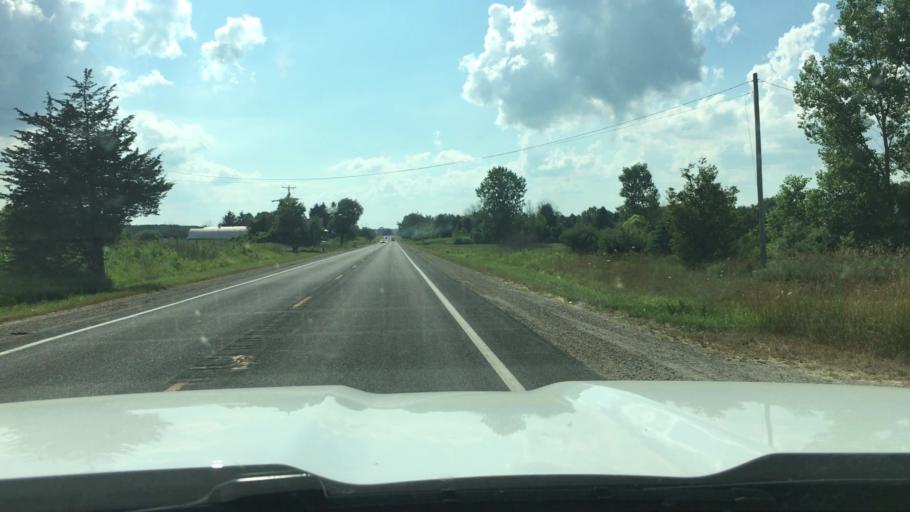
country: US
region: Michigan
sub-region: Montcalm County
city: Stanton
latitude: 43.1776
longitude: -85.0374
